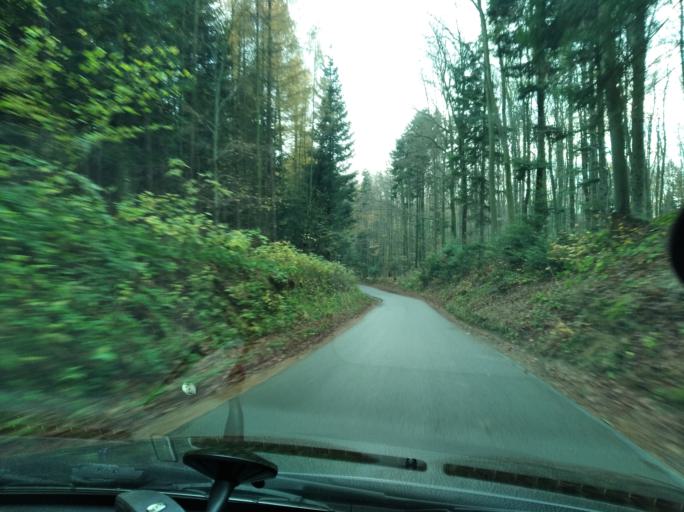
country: PL
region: Subcarpathian Voivodeship
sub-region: Powiat strzyzowski
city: Strzyzow
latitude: 49.9027
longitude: 21.7844
